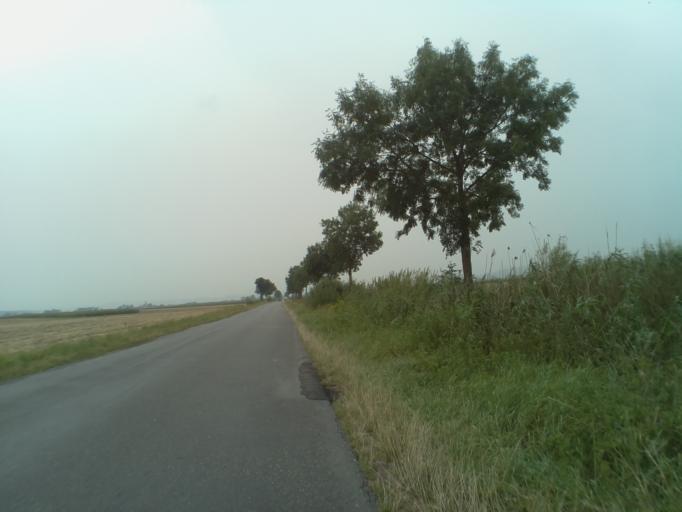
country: PL
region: Lower Silesian Voivodeship
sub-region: Powiat swidnicki
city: Strzegom
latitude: 50.9302
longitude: 16.3245
